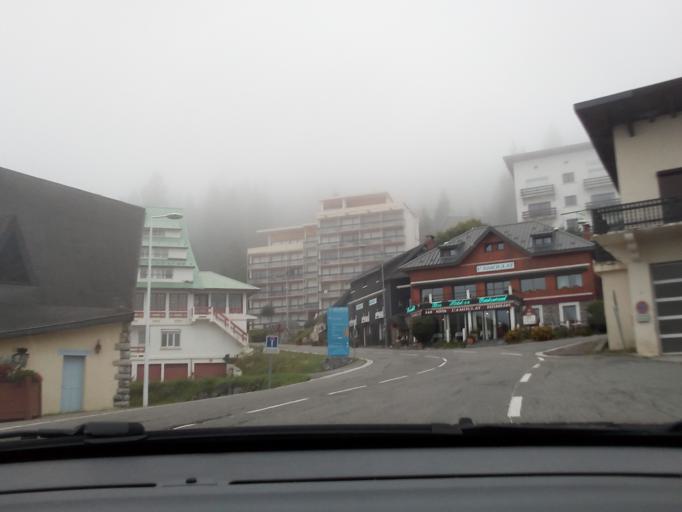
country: FR
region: Aquitaine
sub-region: Departement des Pyrenees-Atlantiques
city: Laruns
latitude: 42.9598
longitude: -0.3324
